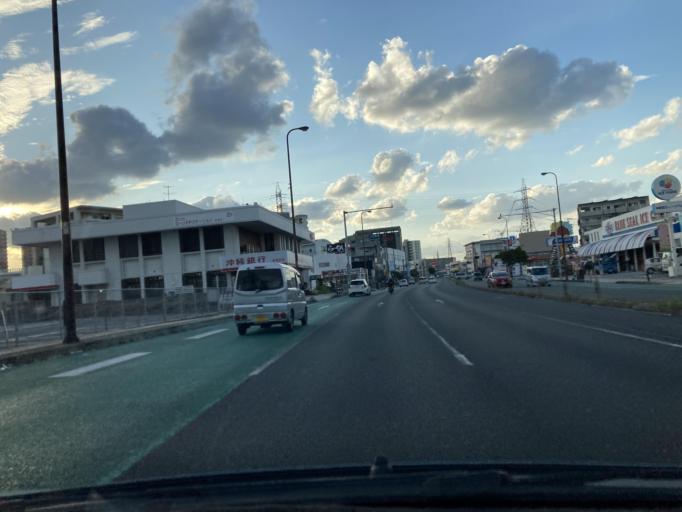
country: JP
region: Okinawa
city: Ginowan
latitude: 26.2665
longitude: 127.7224
